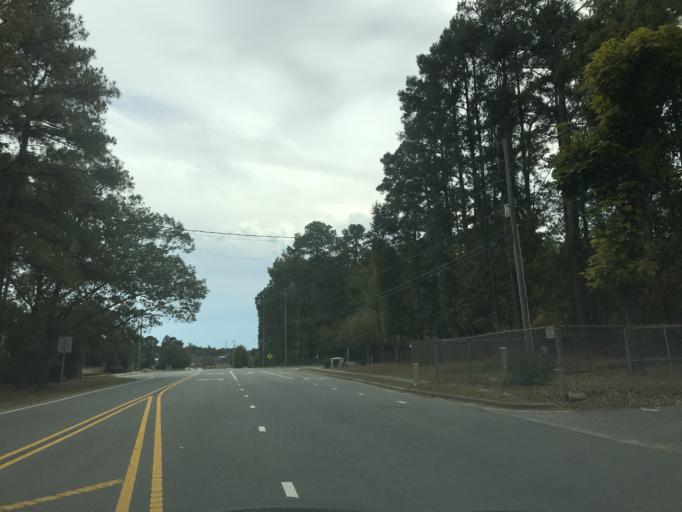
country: US
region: North Carolina
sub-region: Wake County
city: Rolesville
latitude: 35.8874
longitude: -78.5094
